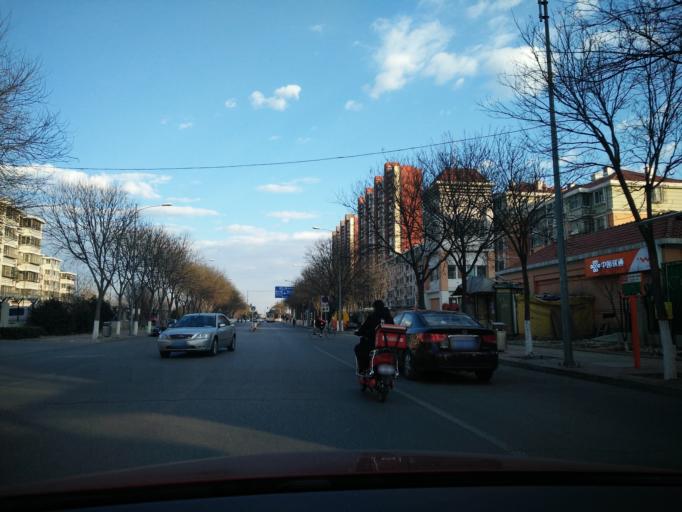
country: CN
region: Beijing
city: Yinghai
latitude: 39.7596
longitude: 116.4941
